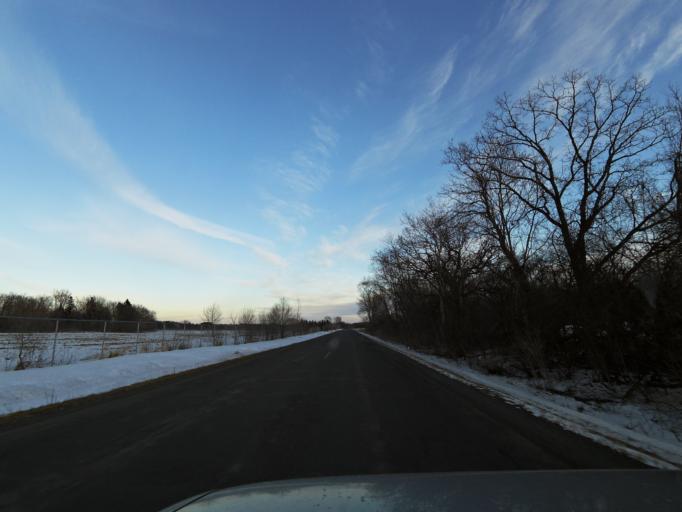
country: US
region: Minnesota
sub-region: Washington County
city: Lake Elmo
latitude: 44.9926
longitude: -92.8496
